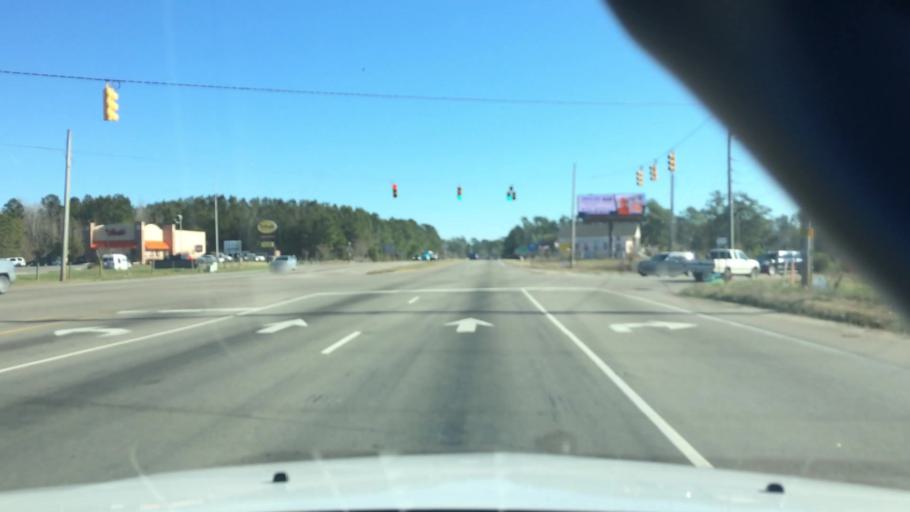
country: US
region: North Carolina
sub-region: Brunswick County
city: Shallotte
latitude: 34.0170
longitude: -78.2736
